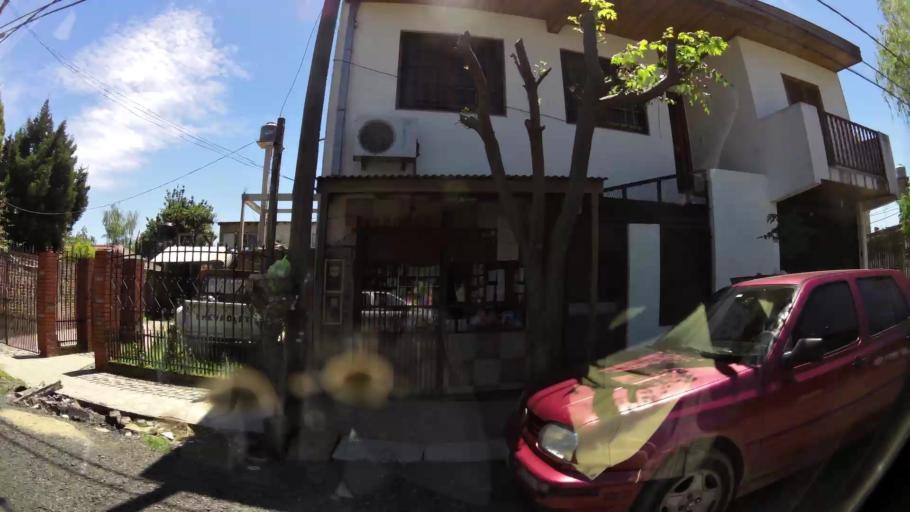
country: AR
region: Buenos Aires
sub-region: Partido de Quilmes
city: Quilmes
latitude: -34.7228
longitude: -58.3236
